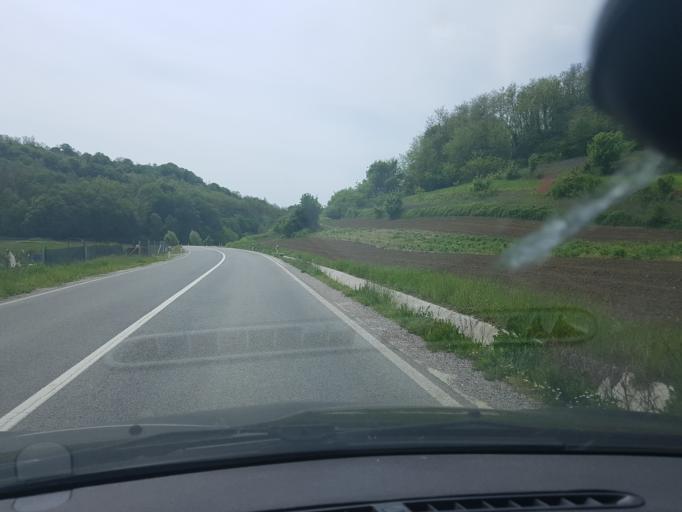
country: HR
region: Krapinsko-Zagorska
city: Pregrada
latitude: 46.1493
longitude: 15.7937
